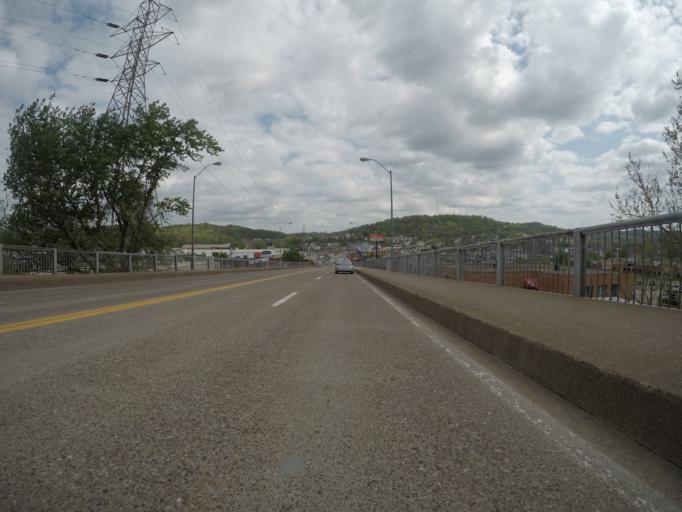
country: US
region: West Virginia
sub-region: Kanawha County
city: South Charleston
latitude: 38.3668
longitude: -81.6682
